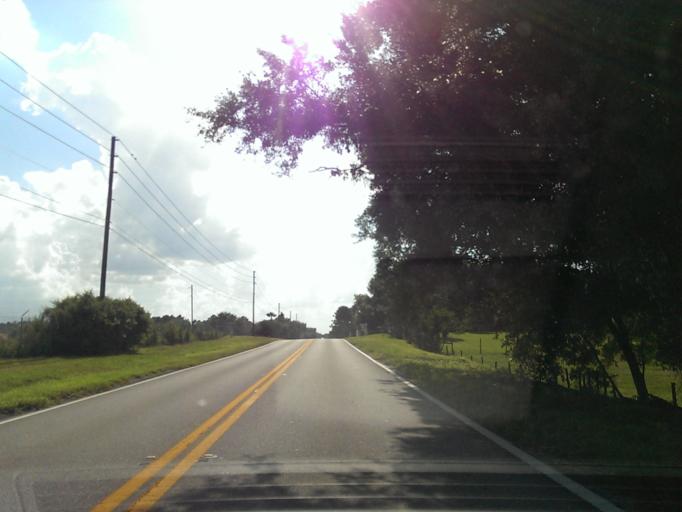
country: US
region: Florida
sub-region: Orange County
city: Oakland
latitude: 28.5073
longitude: -81.6285
